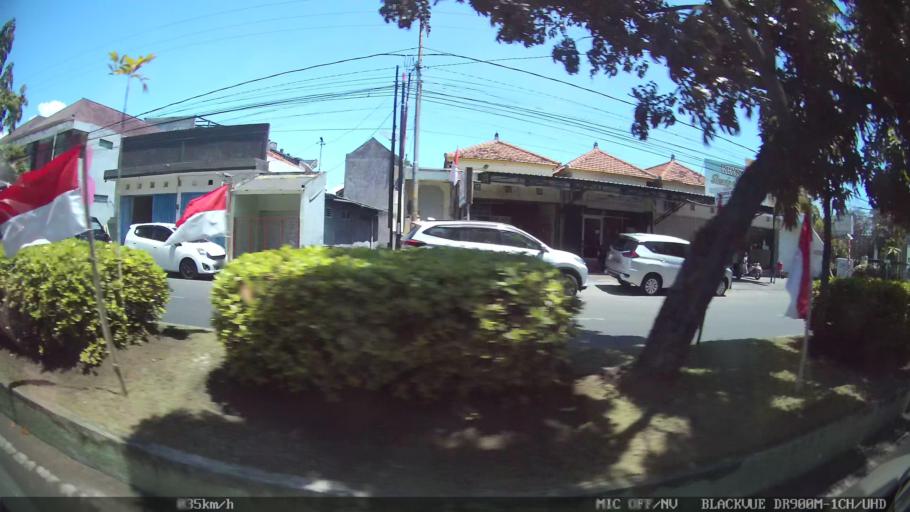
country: ID
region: Bali
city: Banjar Kaliuntu Satu
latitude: -8.1114
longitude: 115.0846
